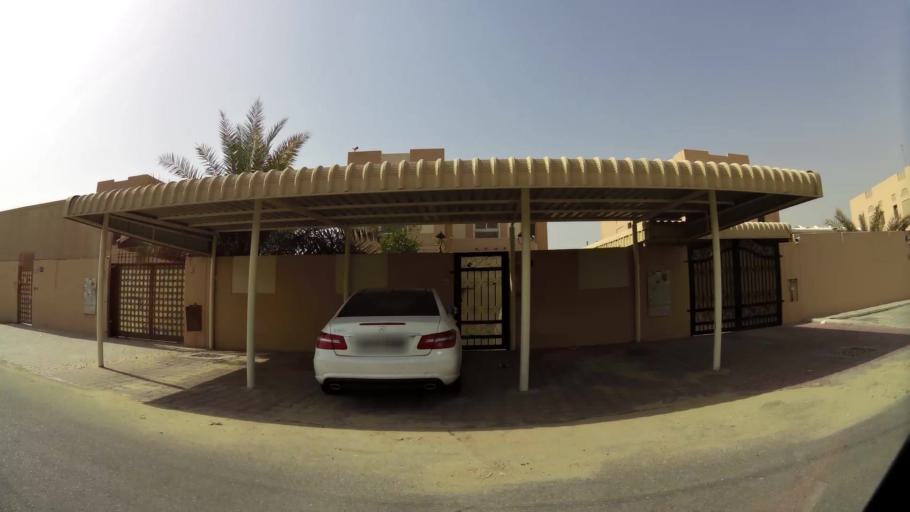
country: AE
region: Ash Shariqah
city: Sharjah
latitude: 25.2643
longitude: 55.4391
